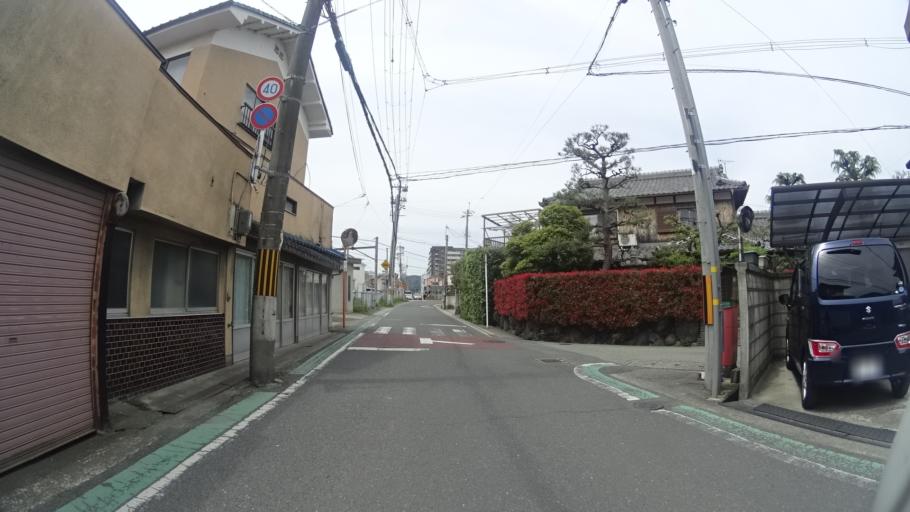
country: JP
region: Kyoto
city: Kameoka
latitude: 35.0308
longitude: 135.5561
